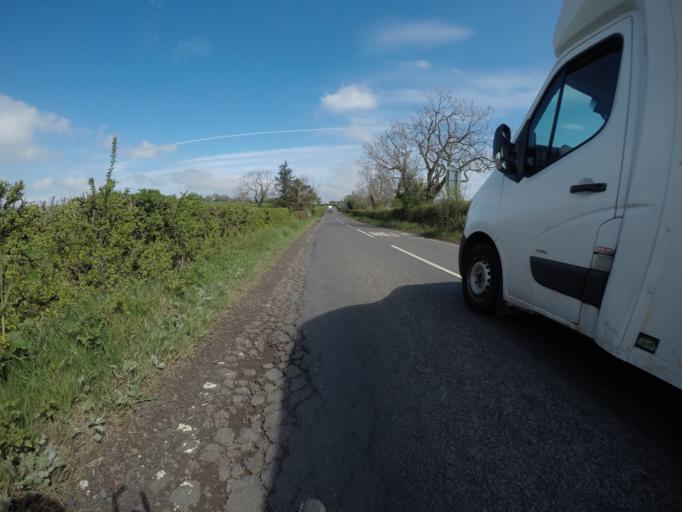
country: GB
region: Scotland
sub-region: East Ayrshire
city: Stewarton
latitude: 55.6665
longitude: -4.5377
